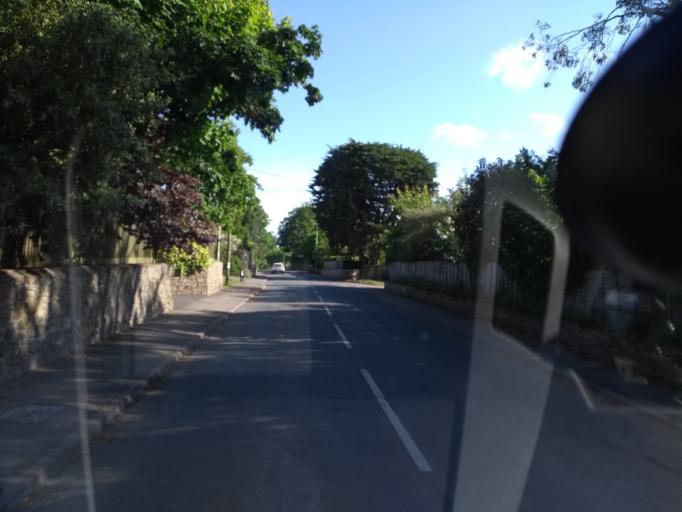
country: GB
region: England
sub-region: Somerset
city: Taunton
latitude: 50.9912
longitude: -3.1225
